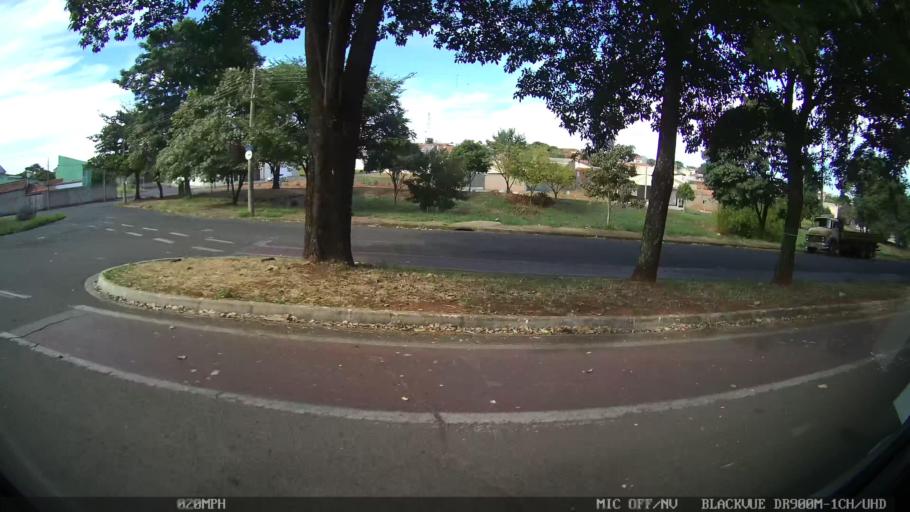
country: BR
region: Sao Paulo
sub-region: Catanduva
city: Catanduva
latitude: -21.1191
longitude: -48.9705
